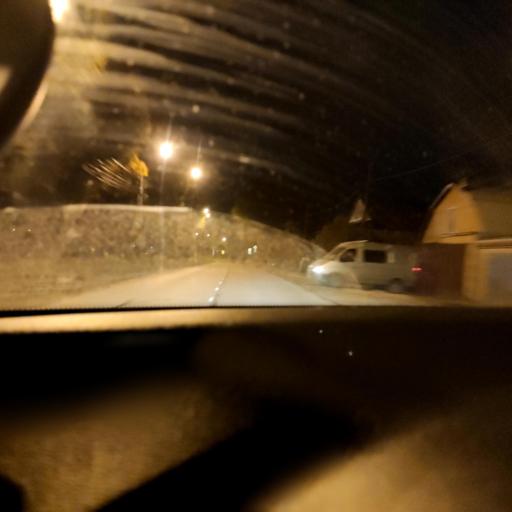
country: RU
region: Samara
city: Smyshlyayevka
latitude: 53.2344
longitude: 50.3071
